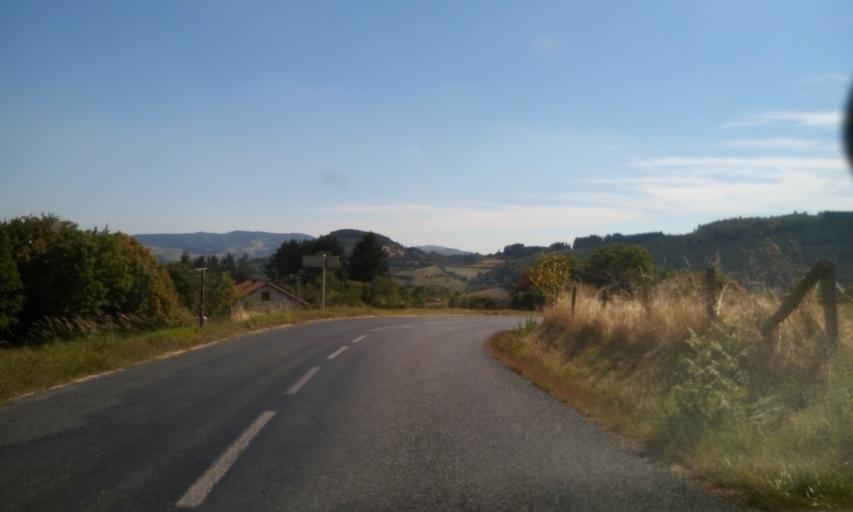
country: FR
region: Rhone-Alpes
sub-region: Departement du Rhone
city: Grandris
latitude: 45.9971
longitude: 4.4338
